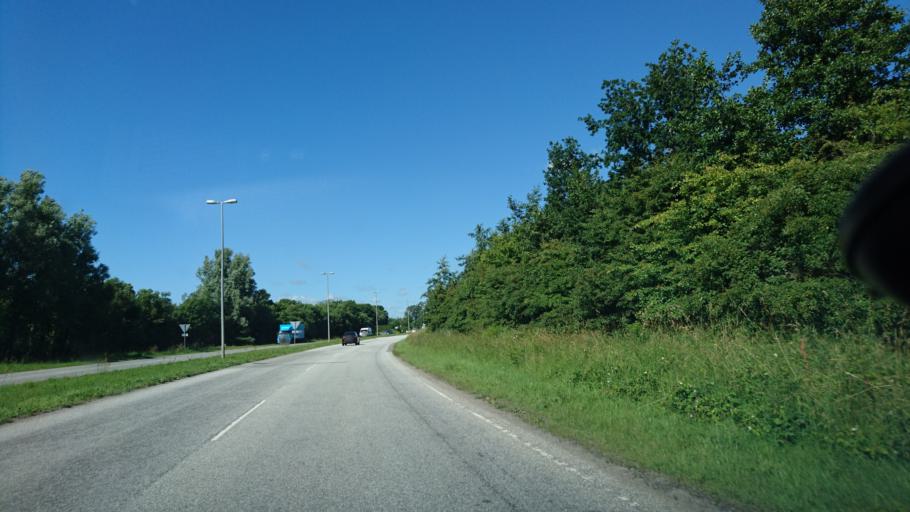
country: DK
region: North Denmark
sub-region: Alborg Kommune
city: Gistrup
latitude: 57.0221
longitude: 10.0052
